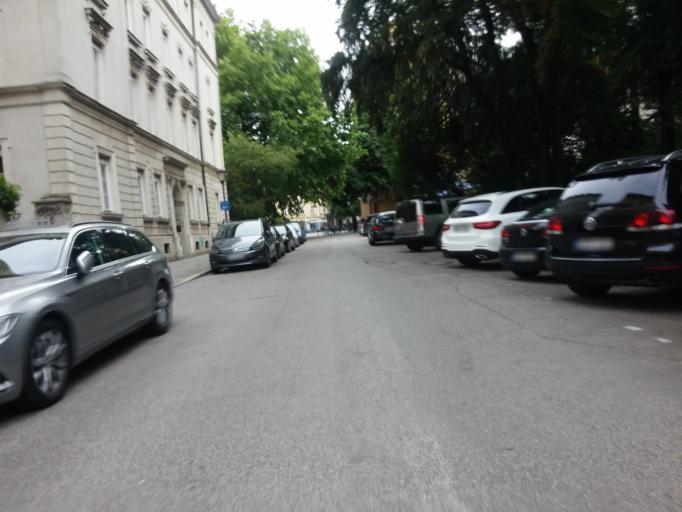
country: DE
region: Bavaria
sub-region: Upper Bavaria
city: Munich
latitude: 48.1354
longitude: 11.5961
